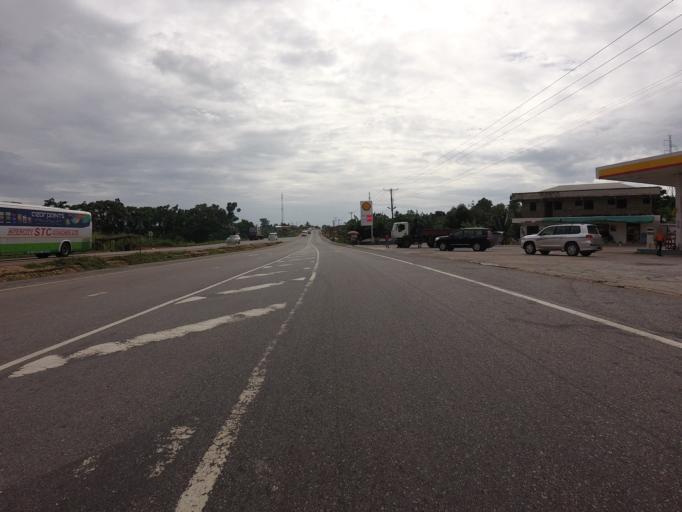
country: GH
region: Eastern
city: Nkawkaw
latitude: 6.5977
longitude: -0.8350
